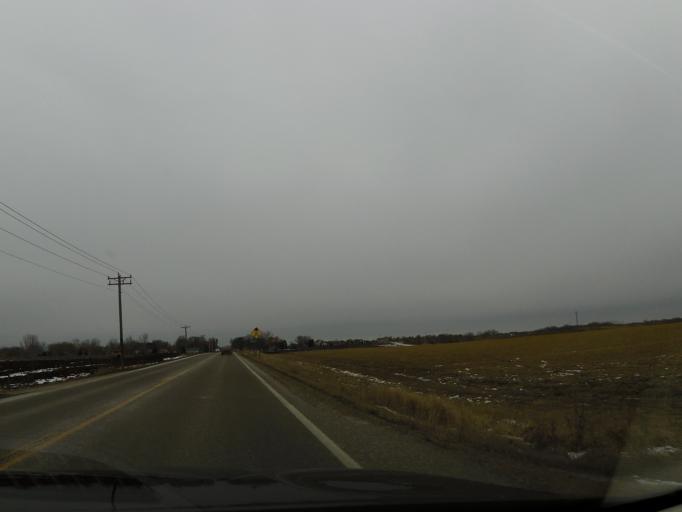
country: US
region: Minnesota
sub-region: Carver County
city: Cologne
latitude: 44.7837
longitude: -93.7881
